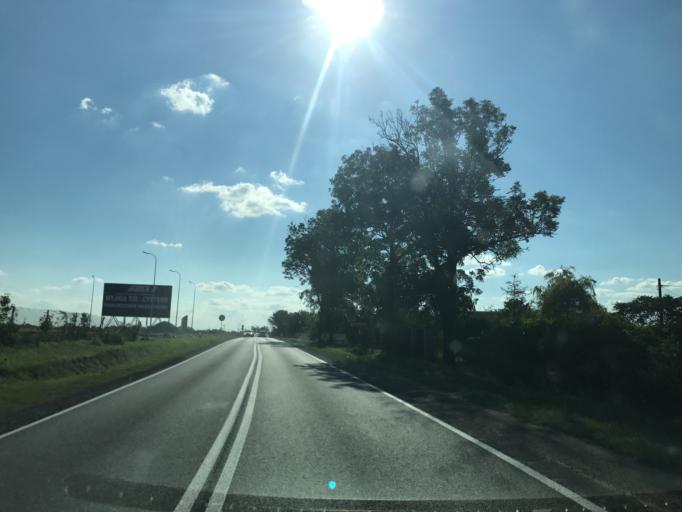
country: PL
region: Kujawsko-Pomorskie
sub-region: Powiat wloclawski
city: Brzesc Kujawski
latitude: 52.6260
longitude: 18.9751
